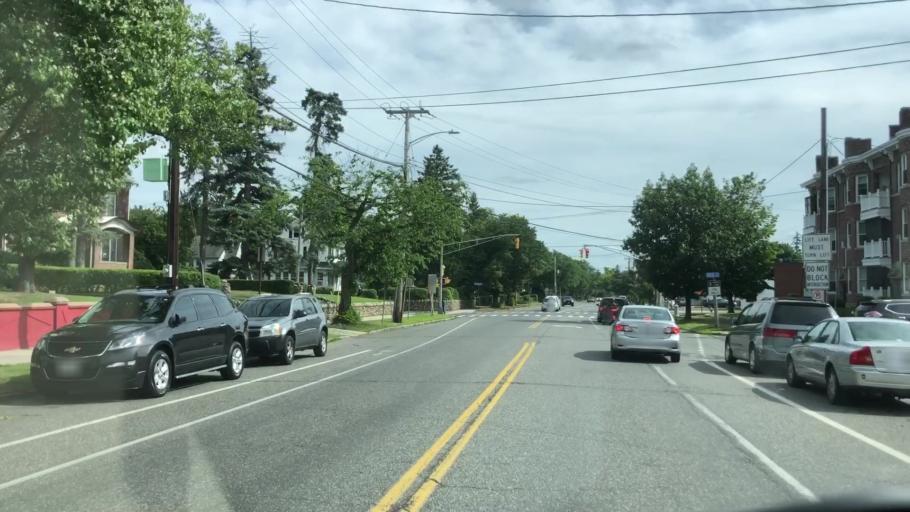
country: US
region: Massachusetts
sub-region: Hampden County
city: Holyoke
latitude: 42.2059
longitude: -72.6308
